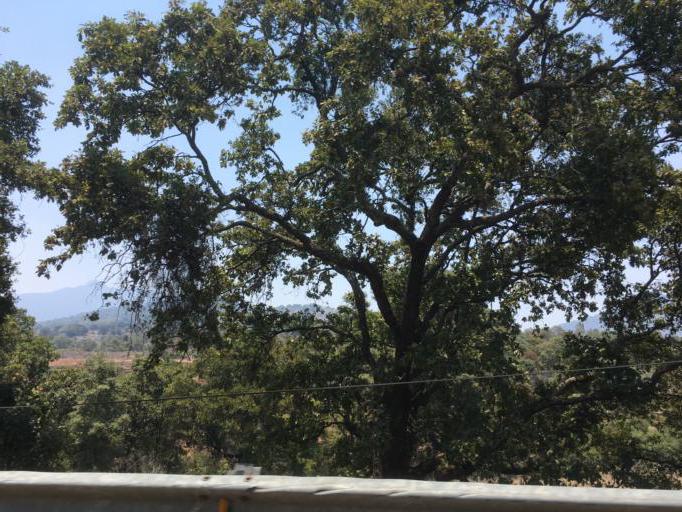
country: MX
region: Michoacan
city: Quiroga
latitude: 19.6567
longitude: -101.5039
